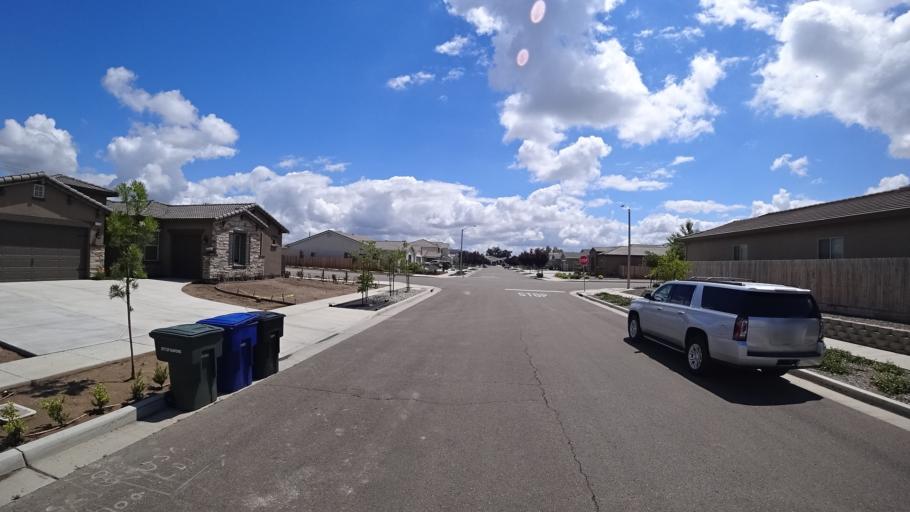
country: US
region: California
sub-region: Kings County
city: Lucerne
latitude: 36.3712
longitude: -119.6623
